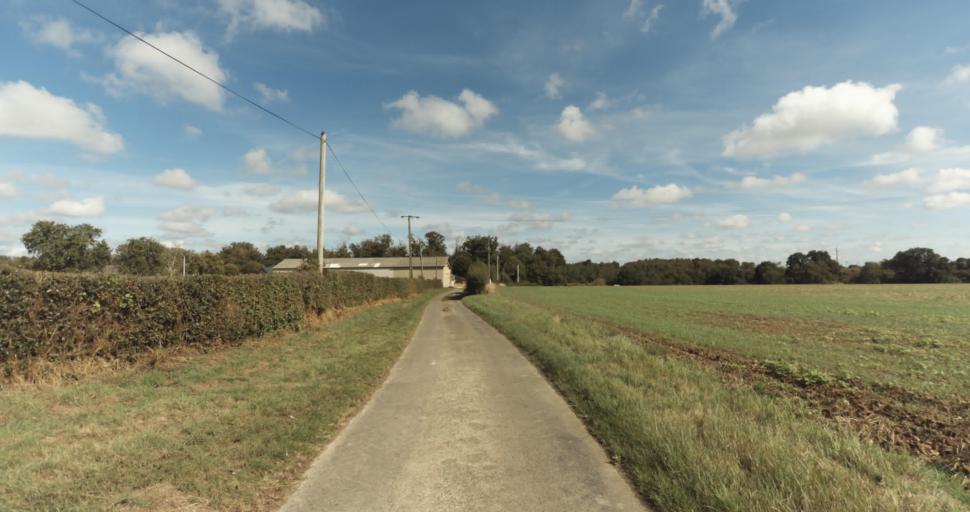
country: FR
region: Lower Normandy
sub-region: Departement du Calvados
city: Orbec
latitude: 48.9467
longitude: 0.3836
